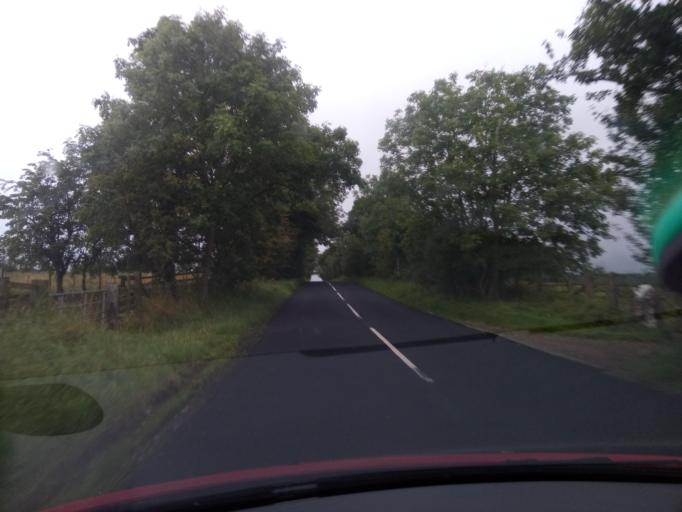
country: GB
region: England
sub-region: Northumberland
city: Rothley
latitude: 55.1994
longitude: -1.9680
